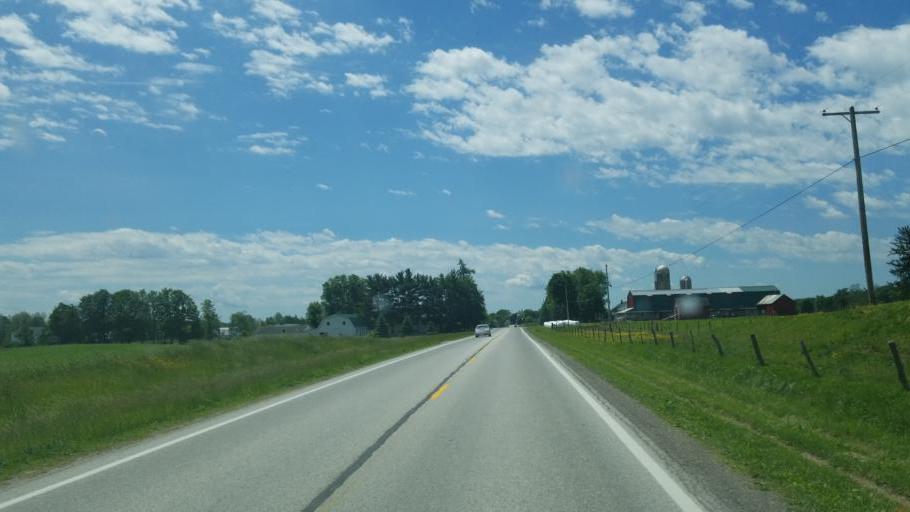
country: US
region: Ohio
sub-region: Geauga County
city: Middlefield
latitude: 41.4345
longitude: -80.9553
